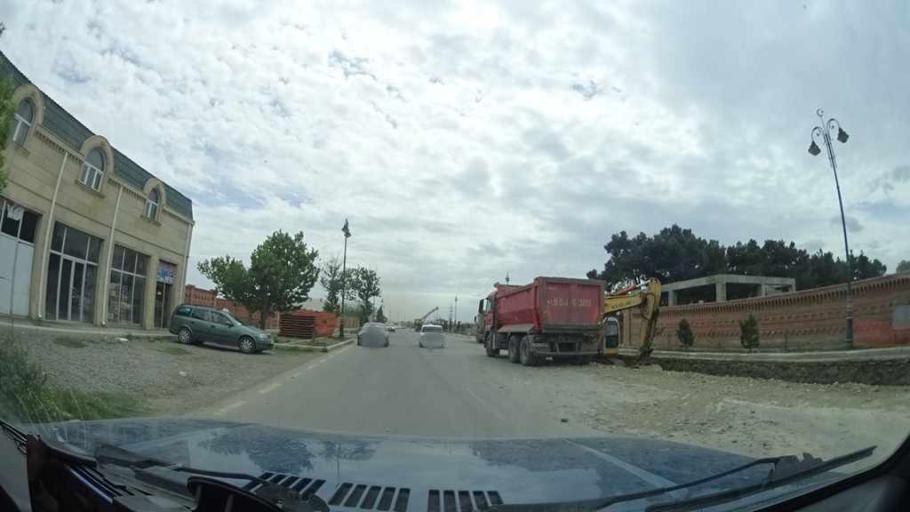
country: AZ
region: Samux
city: Samux
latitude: 40.7187
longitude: 46.4089
